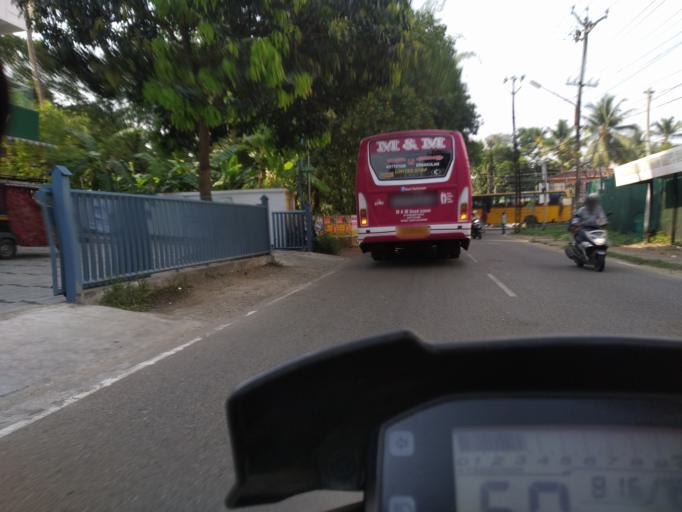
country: IN
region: Kerala
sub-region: Alappuzha
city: Arukutti
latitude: 9.9391
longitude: 76.3514
